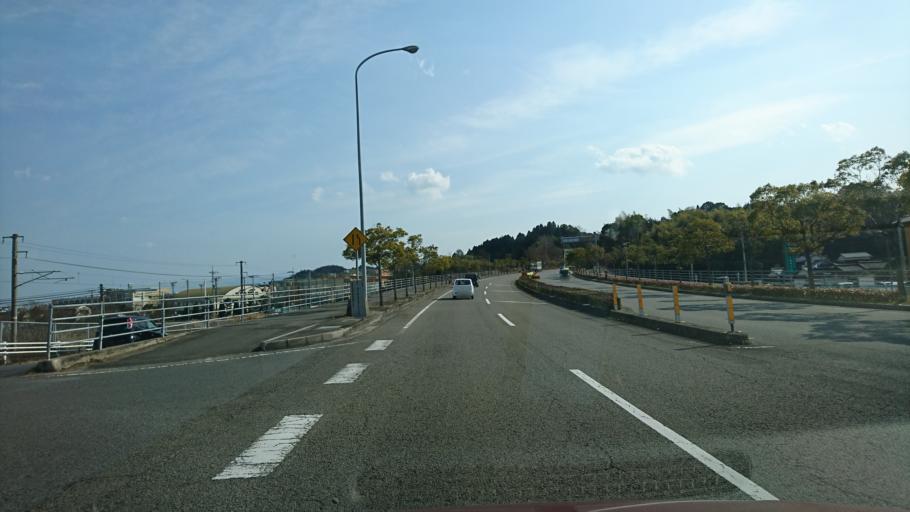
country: JP
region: Ehime
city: Saijo
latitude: 34.0181
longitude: 133.0305
